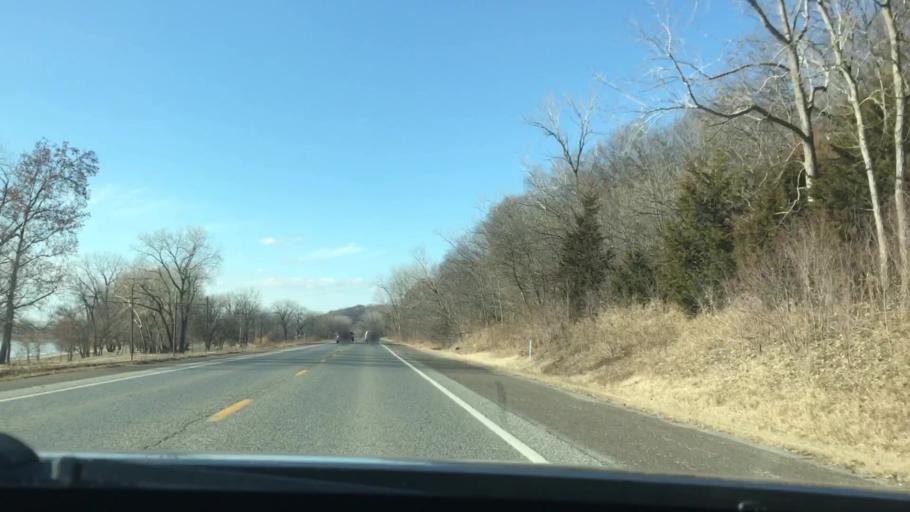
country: US
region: Missouri
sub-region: Platte County
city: Parkville
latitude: 39.1845
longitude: -94.6710
